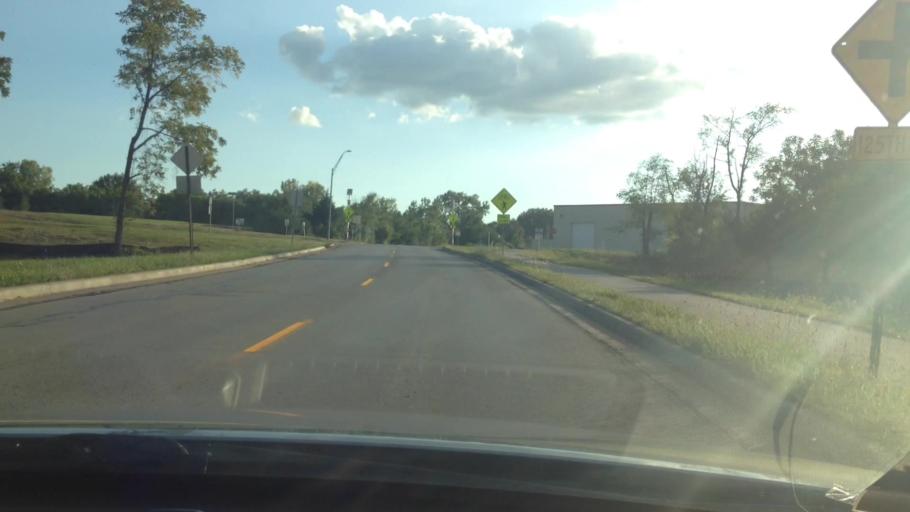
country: US
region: Missouri
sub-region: Jackson County
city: Grandview
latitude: 38.8986
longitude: -94.5202
